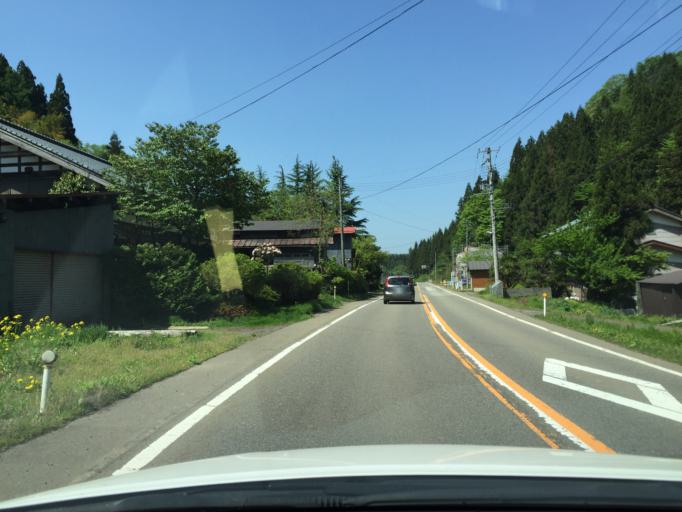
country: JP
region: Niigata
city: Kamo
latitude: 37.6353
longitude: 139.1082
